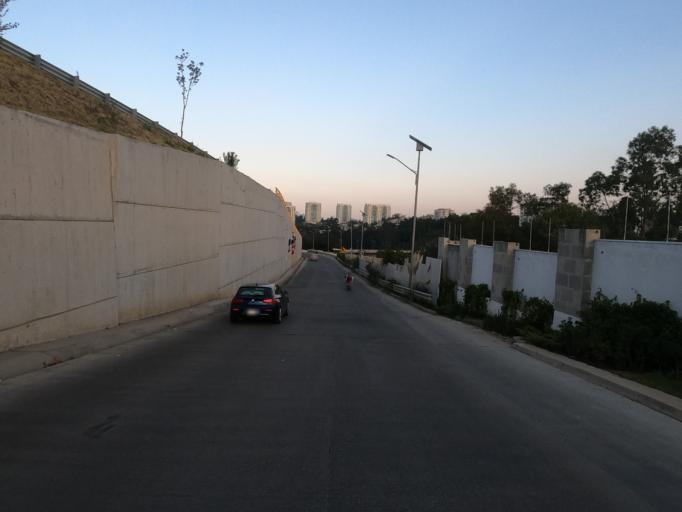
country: MX
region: Mexico
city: San Bartolome Coatepec
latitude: 19.4130
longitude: -99.2888
